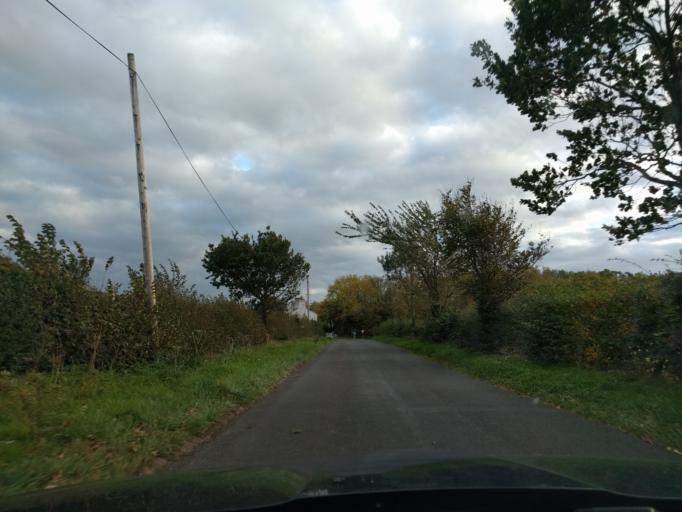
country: GB
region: England
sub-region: Northumberland
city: Ford
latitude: 55.7343
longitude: -2.0958
